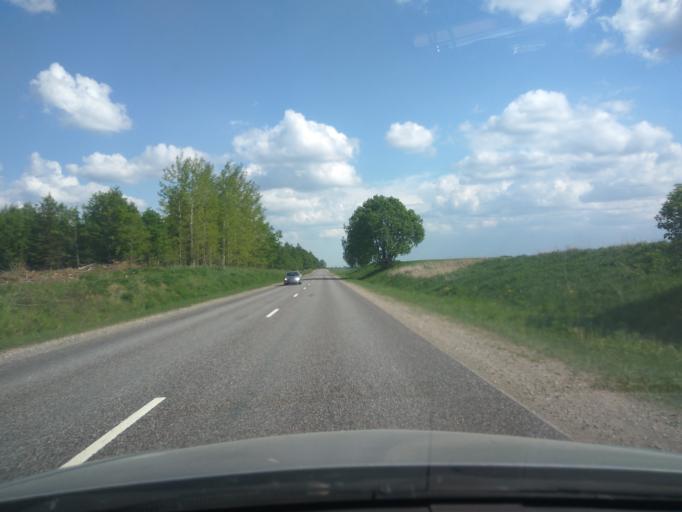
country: LV
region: Kuldigas Rajons
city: Kuldiga
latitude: 57.0306
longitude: 21.8475
